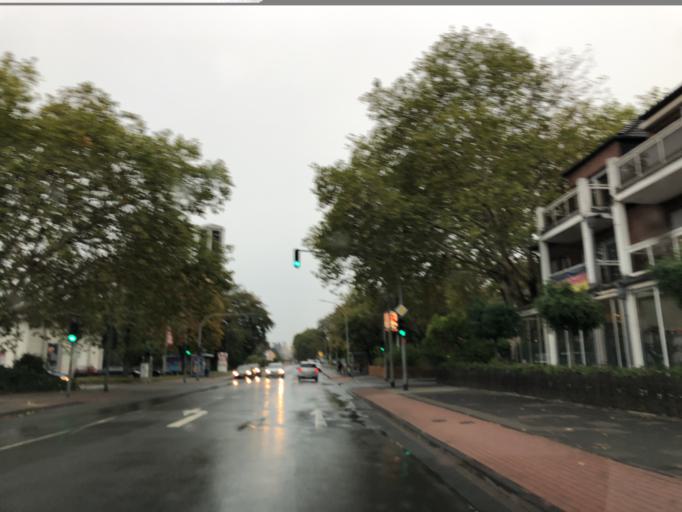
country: DE
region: North Rhine-Westphalia
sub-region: Regierungsbezirk Dusseldorf
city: Hochfeld
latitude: 51.3694
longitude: 6.7372
